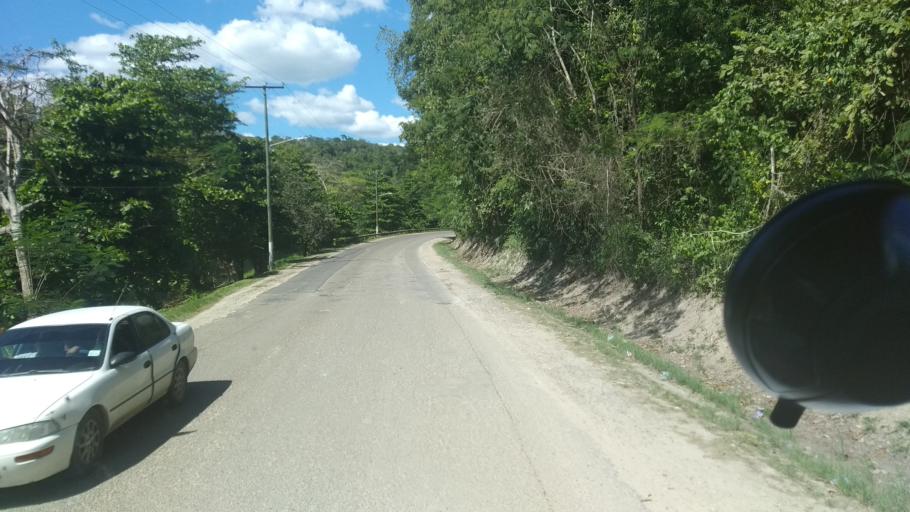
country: BZ
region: Cayo
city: Benque Viejo del Carmen
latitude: 17.0802
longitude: -89.1364
